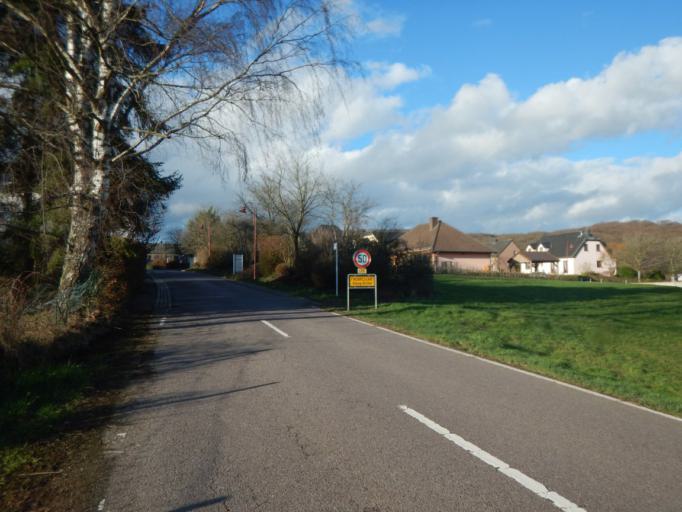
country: BE
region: Wallonia
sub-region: Province du Luxembourg
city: Attert
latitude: 49.7780
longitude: 5.8108
